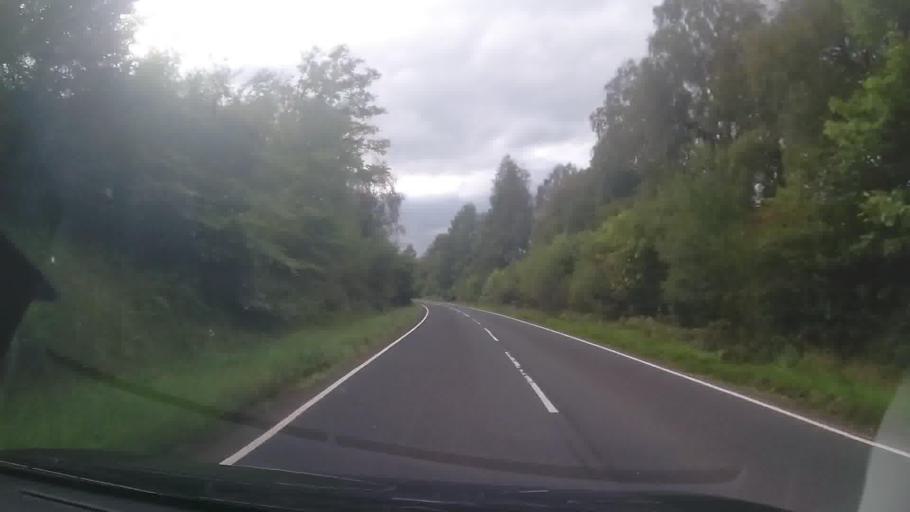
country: GB
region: Scotland
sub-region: Argyll and Bute
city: Garelochhead
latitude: 56.2463
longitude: -4.9382
